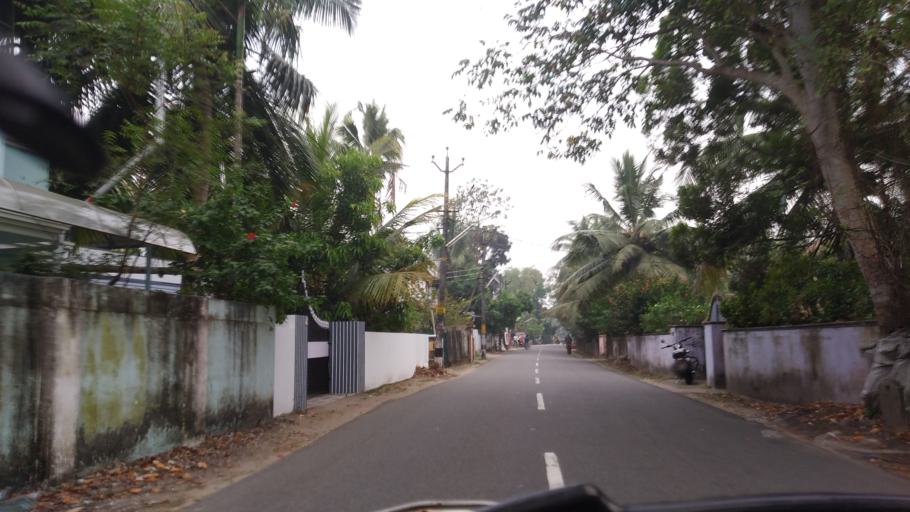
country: IN
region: Kerala
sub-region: Ernakulam
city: Elur
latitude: 10.1449
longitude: 76.2466
